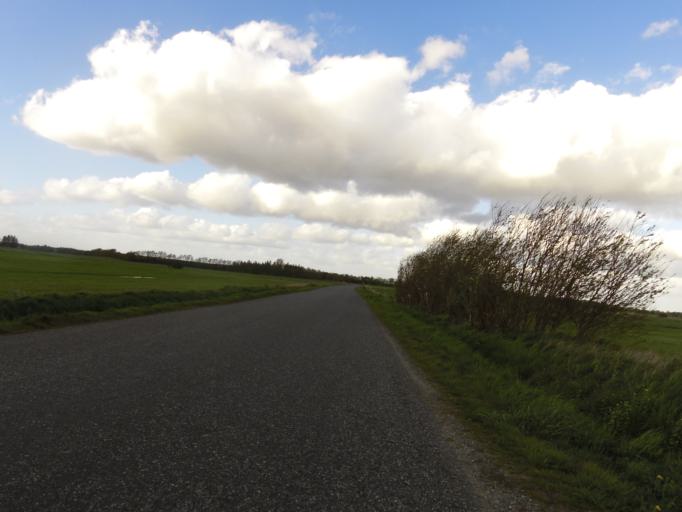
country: DK
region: South Denmark
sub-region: Esbjerg Kommune
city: Ribe
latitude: 55.3283
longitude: 8.8133
